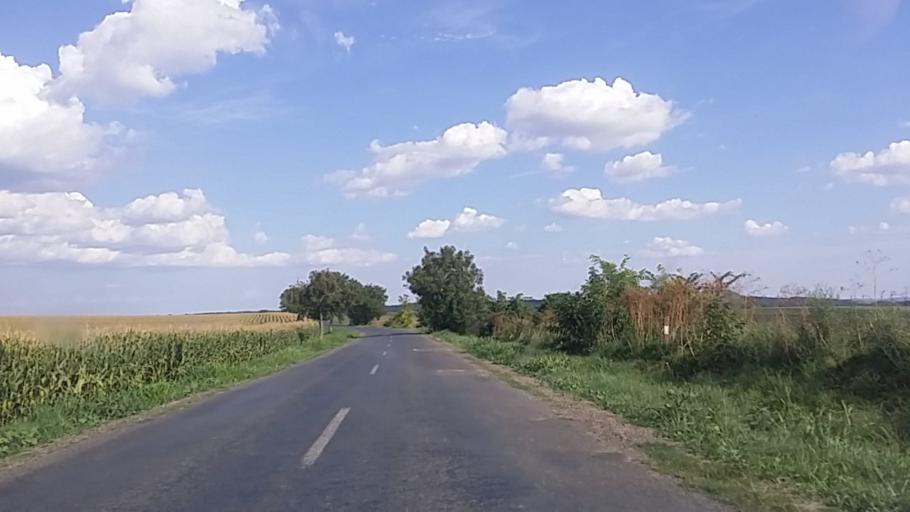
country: HU
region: Tolna
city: Gyonk
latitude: 46.5117
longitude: 18.5423
